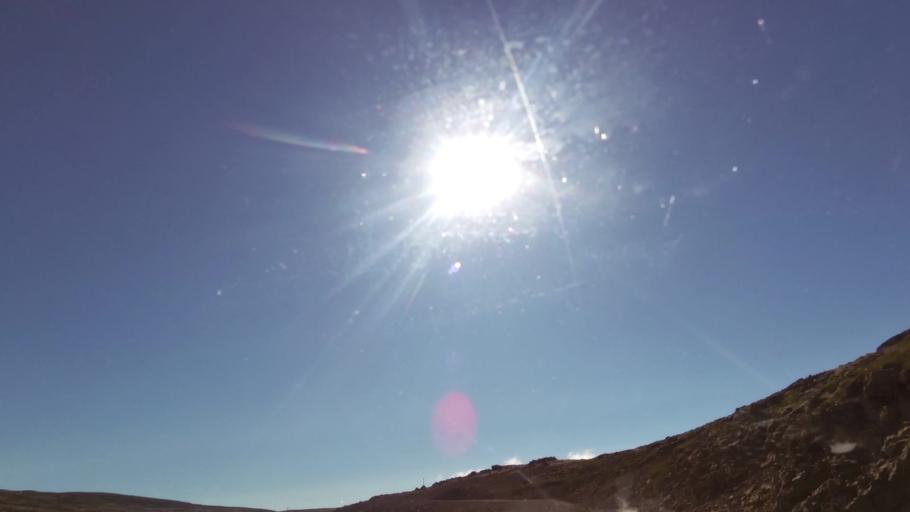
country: IS
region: West
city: Olafsvik
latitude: 65.5541
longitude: -24.1999
